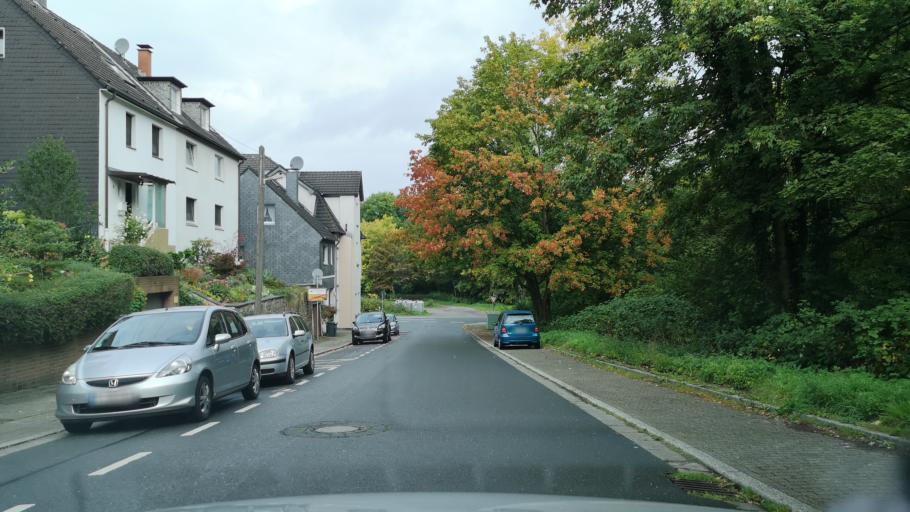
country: DE
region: North Rhine-Westphalia
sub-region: Regierungsbezirk Dusseldorf
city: Heiligenhaus
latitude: 51.3784
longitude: 6.9932
